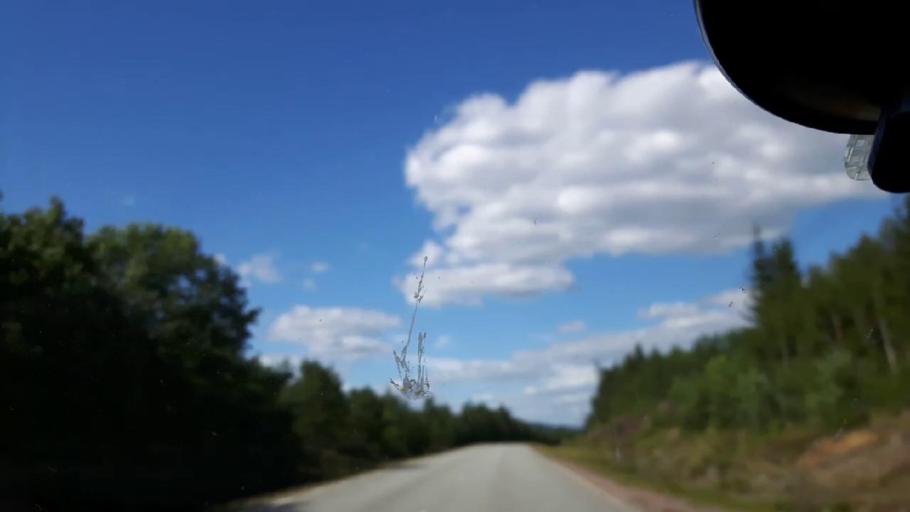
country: SE
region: Vaesternorrland
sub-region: Ange Kommun
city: Fransta
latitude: 62.7167
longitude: 16.3344
